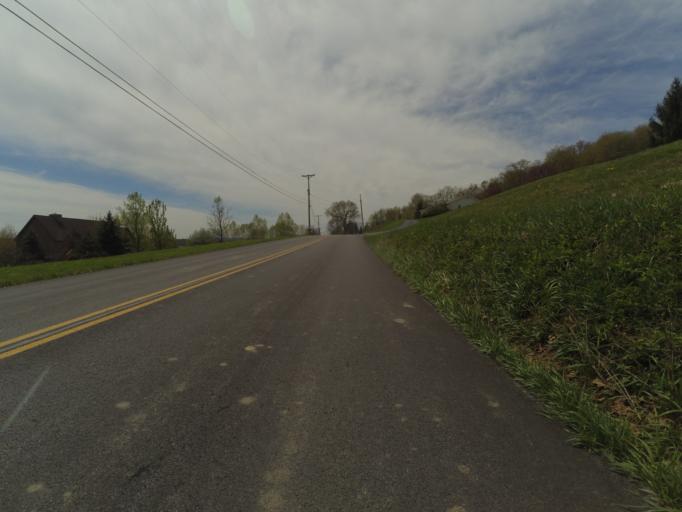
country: US
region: Pennsylvania
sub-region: Blair County
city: Tyrone
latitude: 40.7168
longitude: -78.1347
